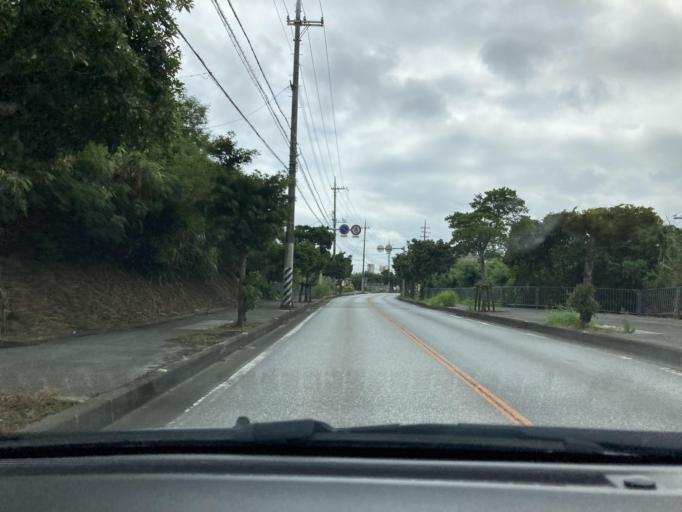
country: JP
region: Okinawa
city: Ginowan
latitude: 26.2593
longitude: 127.7765
